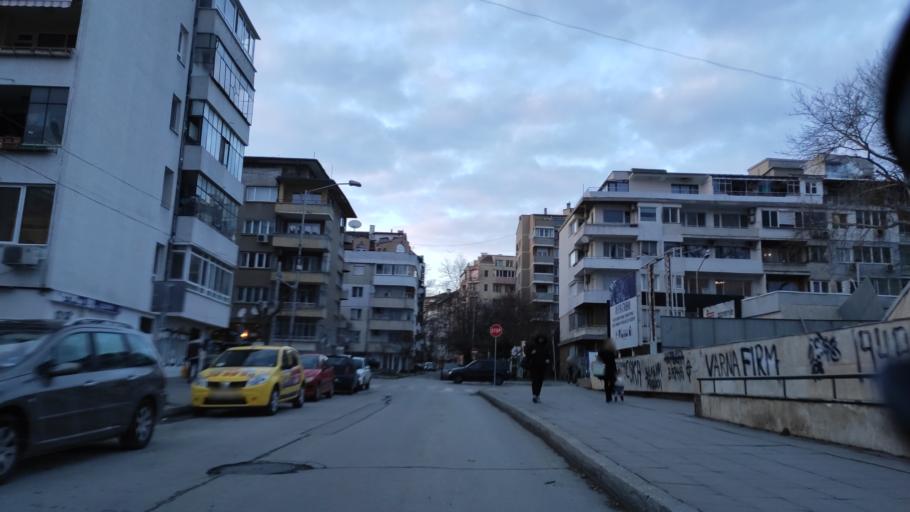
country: BG
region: Varna
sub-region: Obshtina Varna
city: Varna
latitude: 43.2108
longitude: 27.9296
